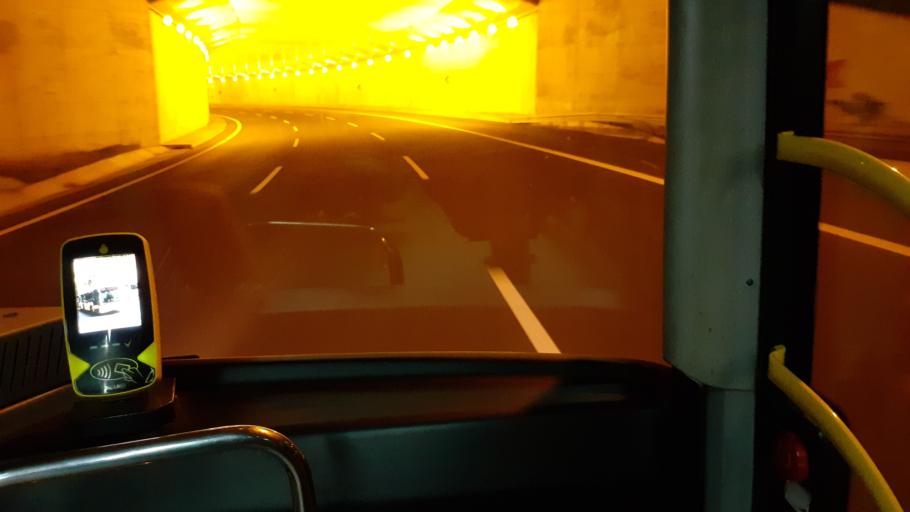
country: TR
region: Istanbul
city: Durusu
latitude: 41.2439
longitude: 28.7391
